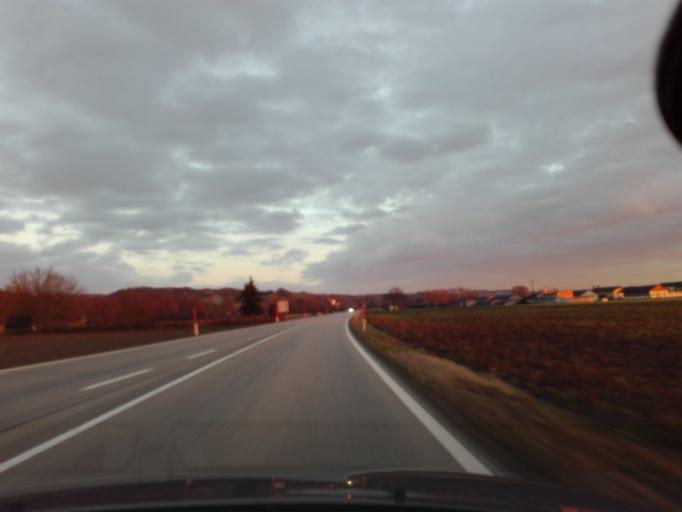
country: AT
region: Upper Austria
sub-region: Politischer Bezirk Perg
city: Bad Kreuzen
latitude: 48.2115
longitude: 14.7719
